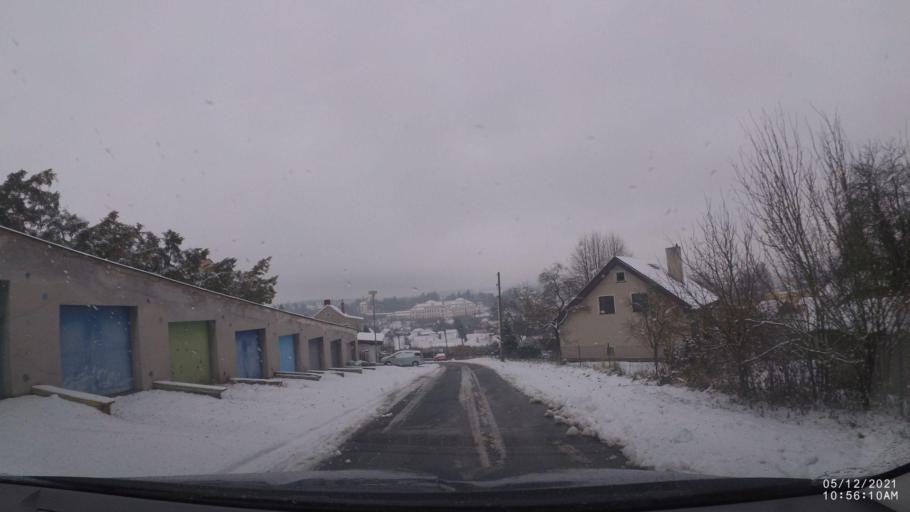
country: CZ
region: Kralovehradecky
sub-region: Okres Rychnov nad Kneznou
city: Rychnov nad Kneznou
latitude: 50.1665
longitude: 16.2671
